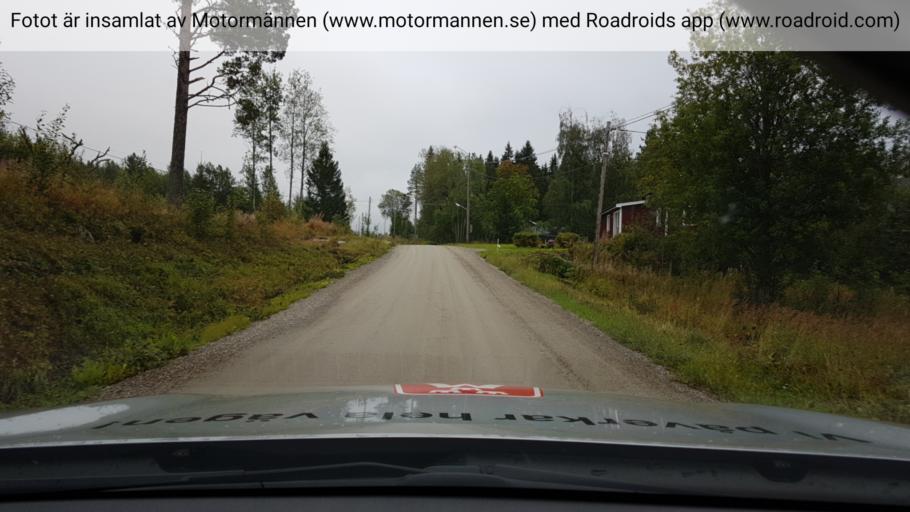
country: SE
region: Jaemtland
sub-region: Braecke Kommun
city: Braecke
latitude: 62.7739
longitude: 15.4801
